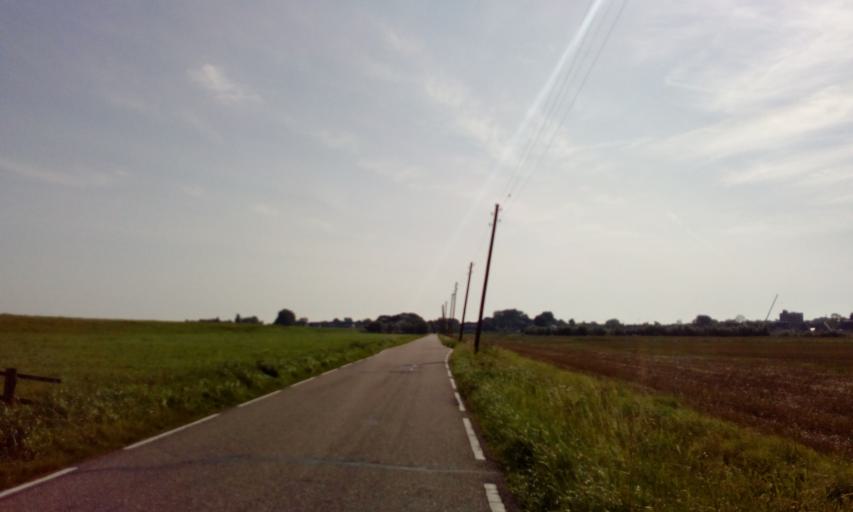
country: NL
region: South Holland
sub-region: Gemeente Waddinxveen
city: Groenswaard
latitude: 52.0466
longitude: 4.6276
